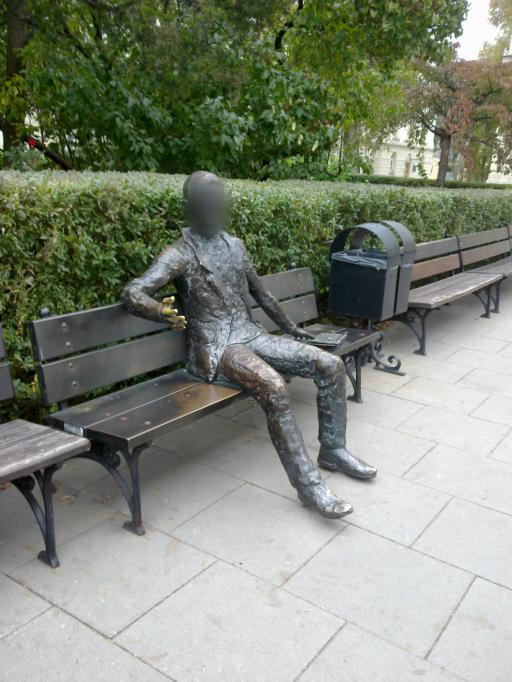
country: PL
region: Masovian Voivodeship
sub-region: Warszawa
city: Srodmiescie
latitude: 52.2403
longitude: 21.0188
